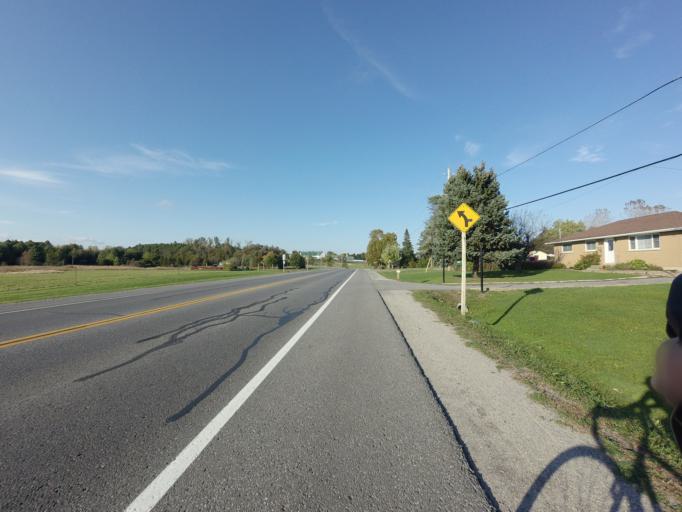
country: CA
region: Ontario
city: Kingston
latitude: 44.3084
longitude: -76.4647
